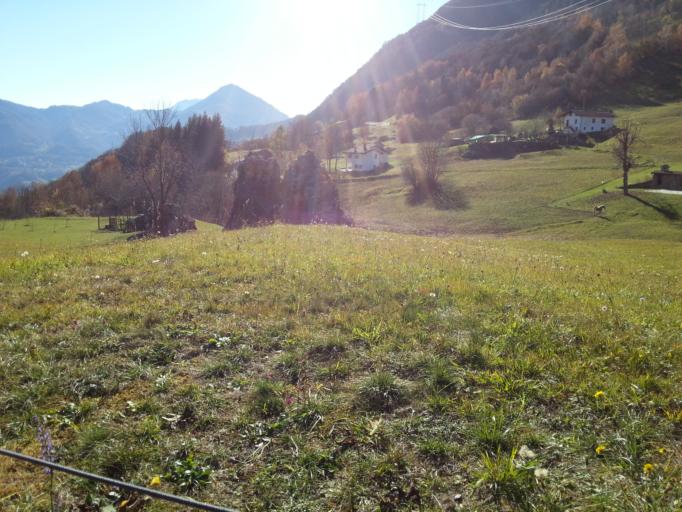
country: IT
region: Lombardy
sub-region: Provincia di Lecco
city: Pasturo
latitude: 45.9652
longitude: 9.4329
